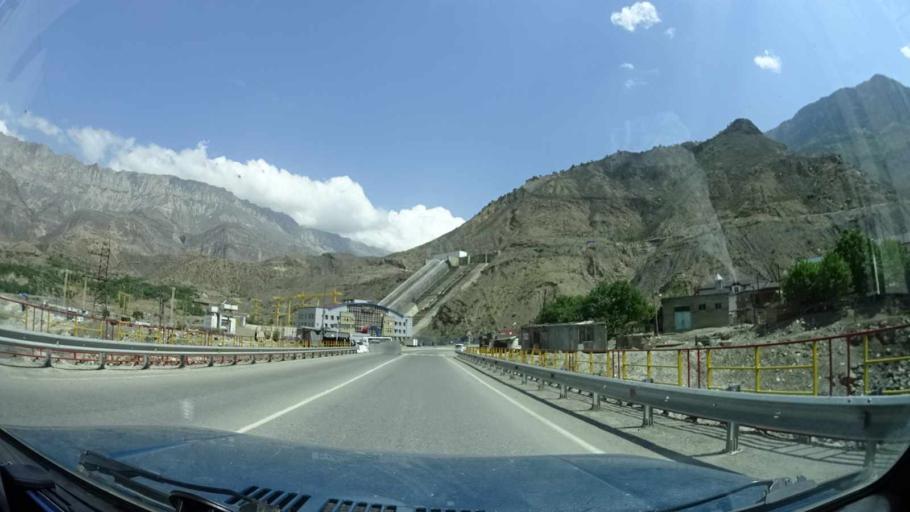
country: RU
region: Dagestan
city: Gimry
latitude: 42.7446
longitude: 46.8289
